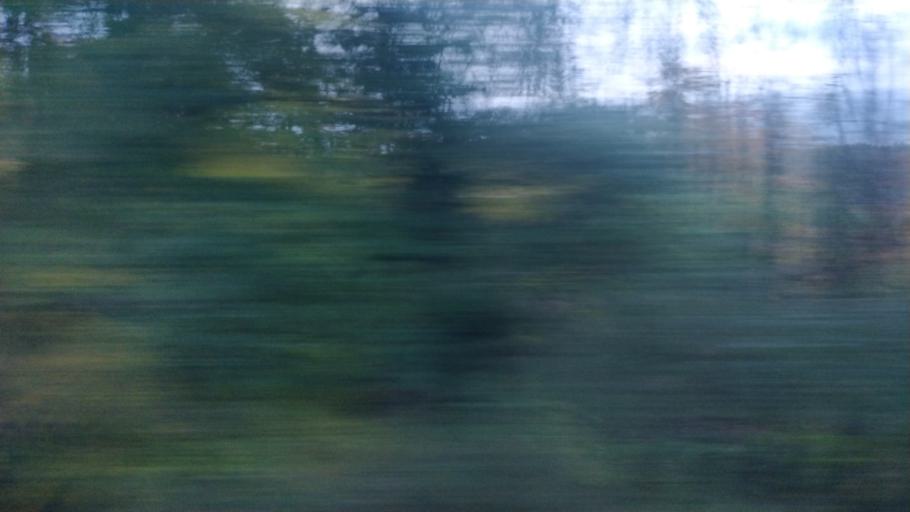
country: GB
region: England
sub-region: Lancashire
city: Appley Bridge
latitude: 53.5828
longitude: -2.7351
